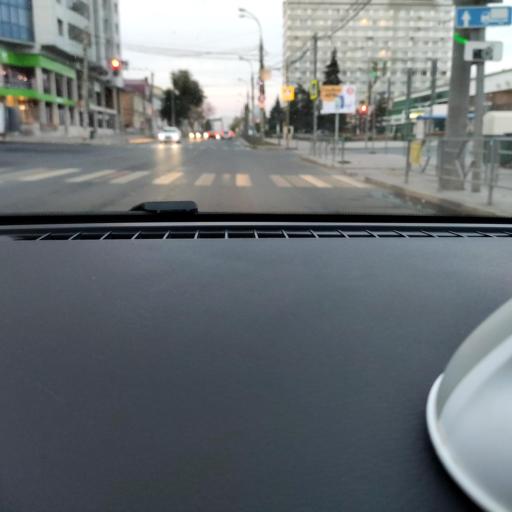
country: RU
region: Samara
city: Rozhdestveno
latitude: 53.1877
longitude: 50.0803
